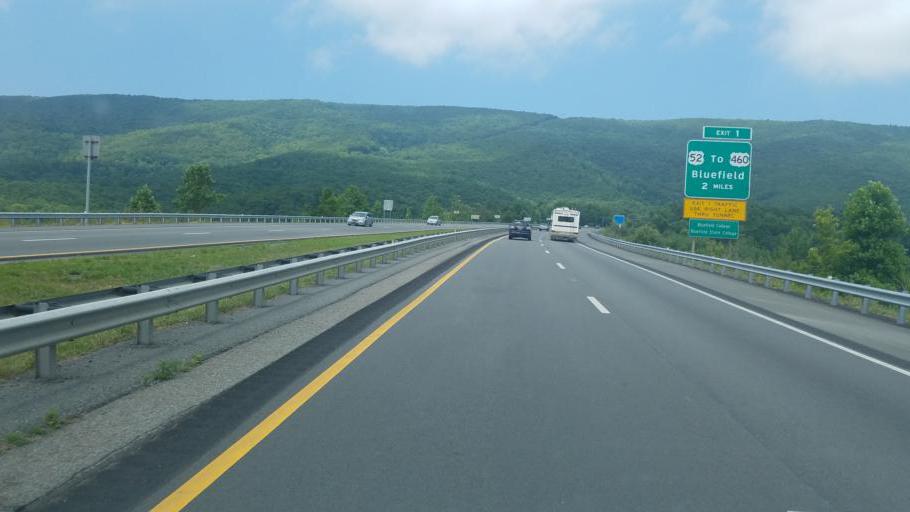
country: US
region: West Virginia
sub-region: Mercer County
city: Bluefield
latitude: 37.2565
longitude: -81.1193
